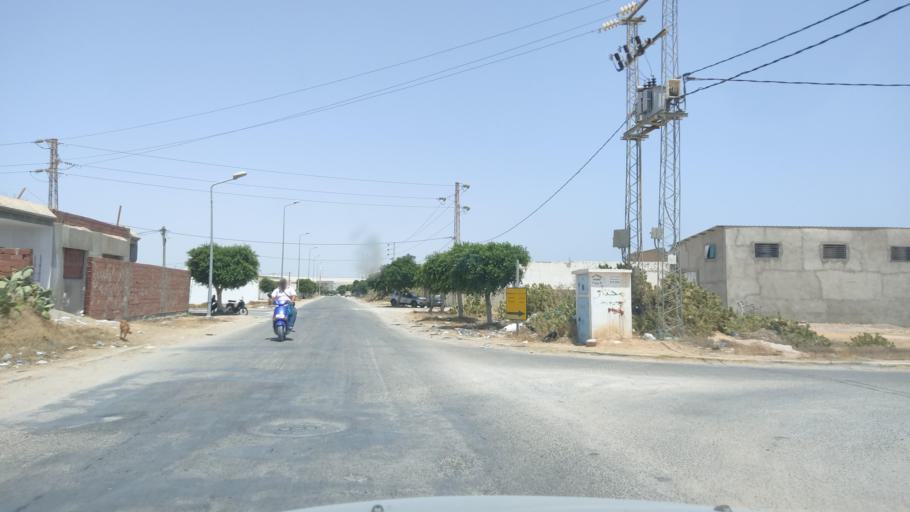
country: TN
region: Safaqis
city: Sfax
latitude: 34.6801
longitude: 10.7202
